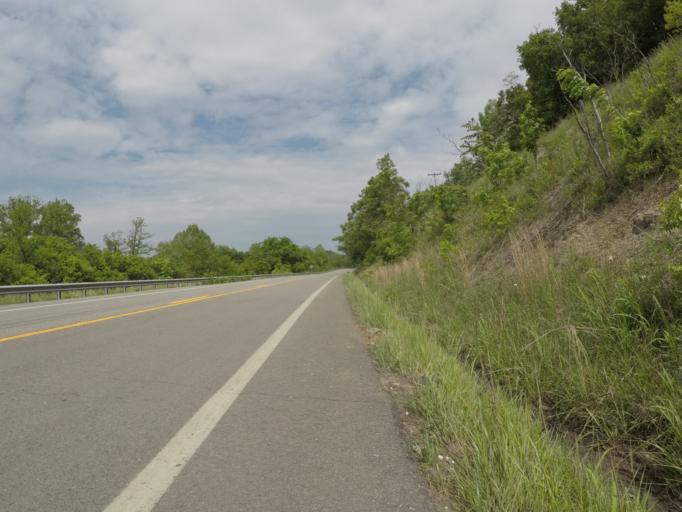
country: US
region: West Virginia
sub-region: Wayne County
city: Kenova
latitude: 38.3402
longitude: -82.5858
